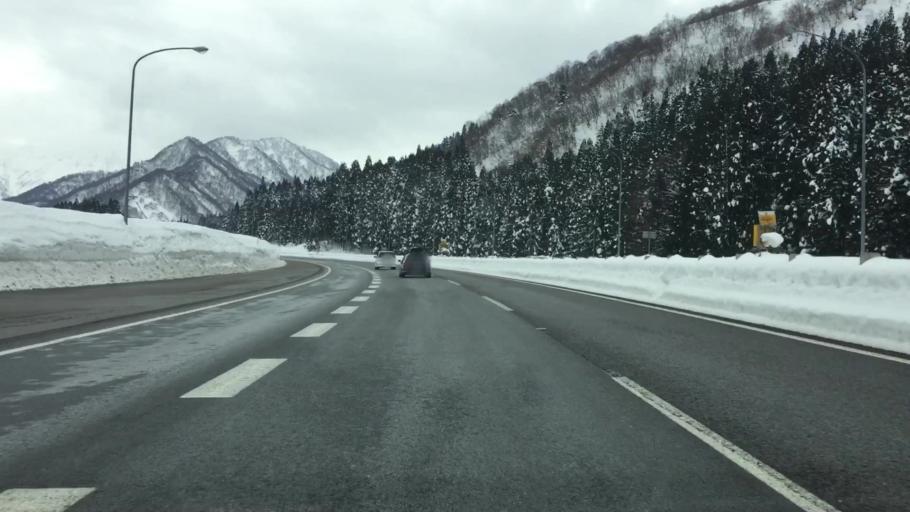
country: JP
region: Niigata
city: Shiozawa
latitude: 36.8948
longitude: 138.8454
